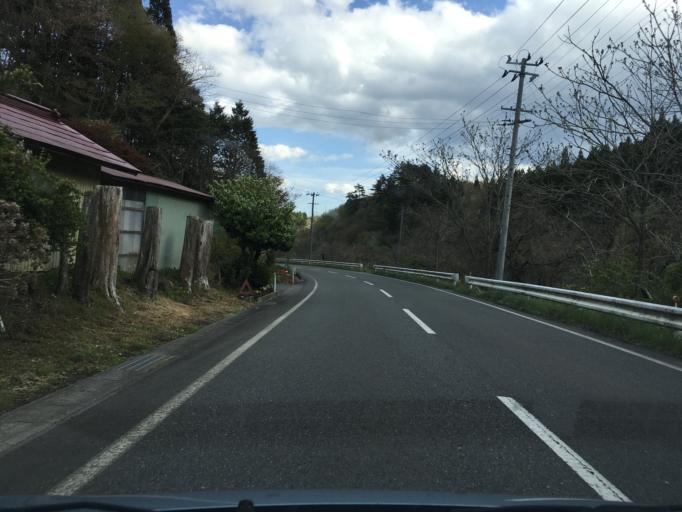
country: JP
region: Iwate
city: Ichinoseki
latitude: 38.8062
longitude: 141.3836
